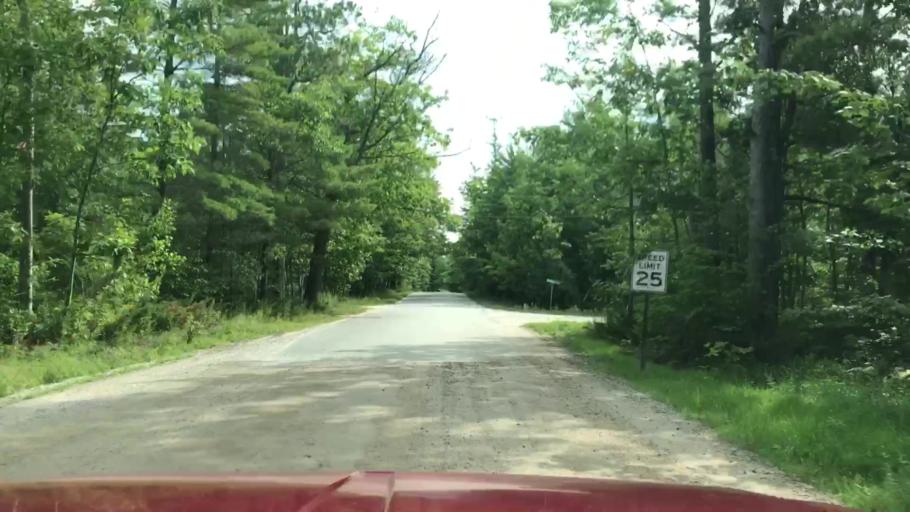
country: US
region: Michigan
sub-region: Charlevoix County
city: Charlevoix
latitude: 45.7468
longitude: -85.5275
